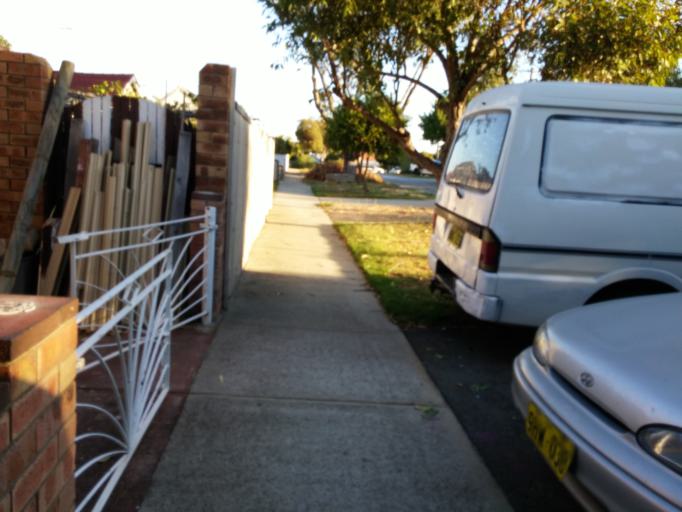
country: AU
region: Western Australia
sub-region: Fremantle
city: White Gum Valley
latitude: -32.0575
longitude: 115.7671
